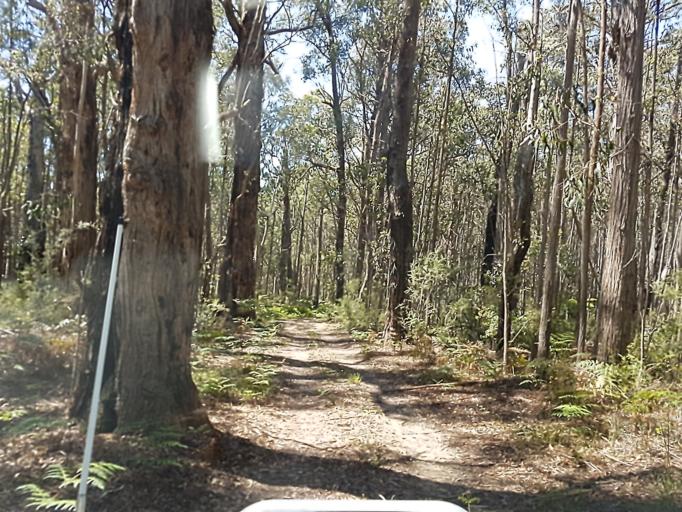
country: AU
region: Victoria
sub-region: East Gippsland
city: Lakes Entrance
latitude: -37.2931
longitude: 148.3252
